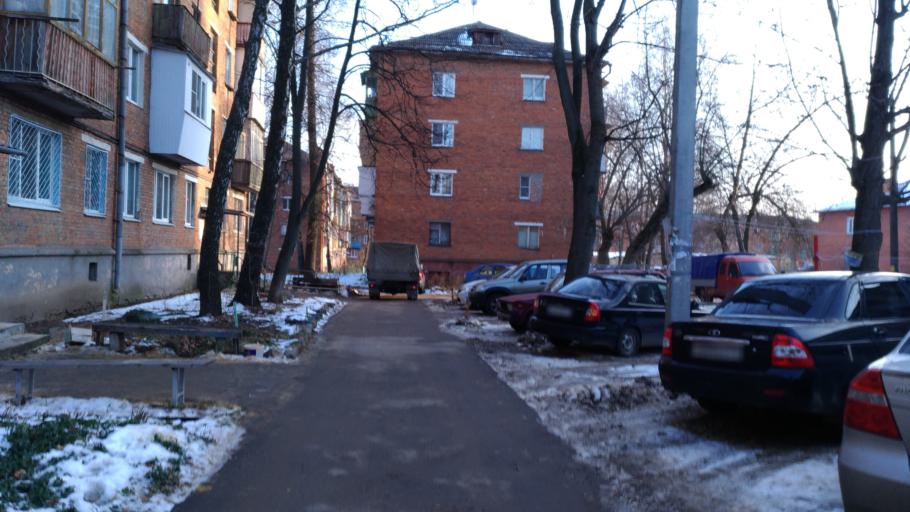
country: RU
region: Tula
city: Tula
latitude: 54.1900
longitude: 37.6974
